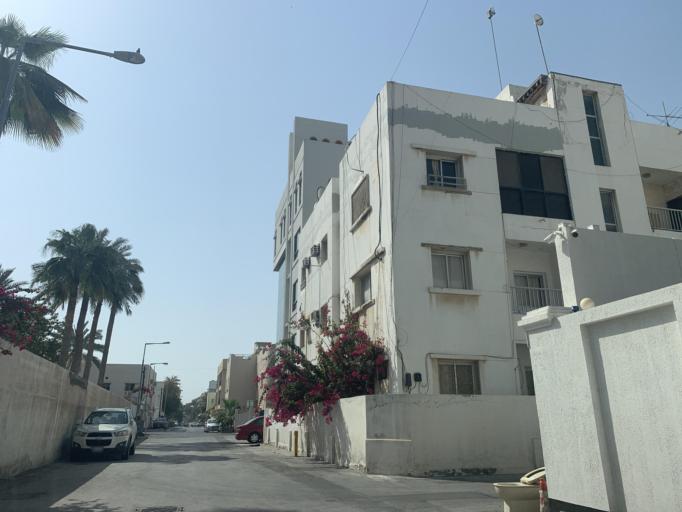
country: BH
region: Manama
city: Jidd Hafs
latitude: 26.2235
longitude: 50.5658
